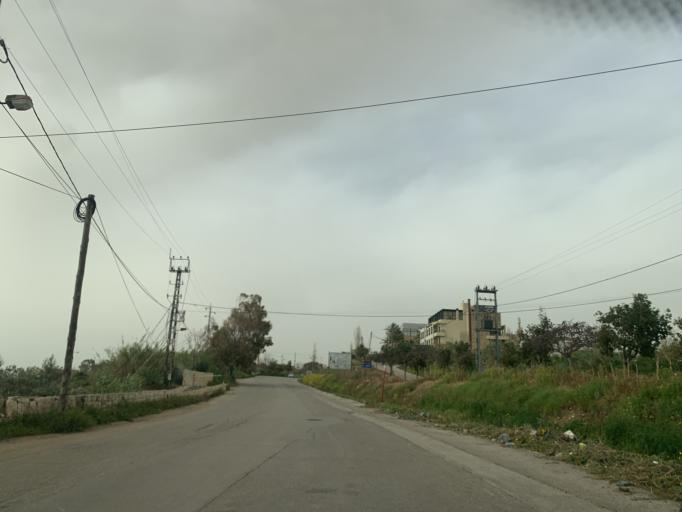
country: LB
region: Mont-Liban
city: Jbail
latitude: 34.1054
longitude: 35.6519
